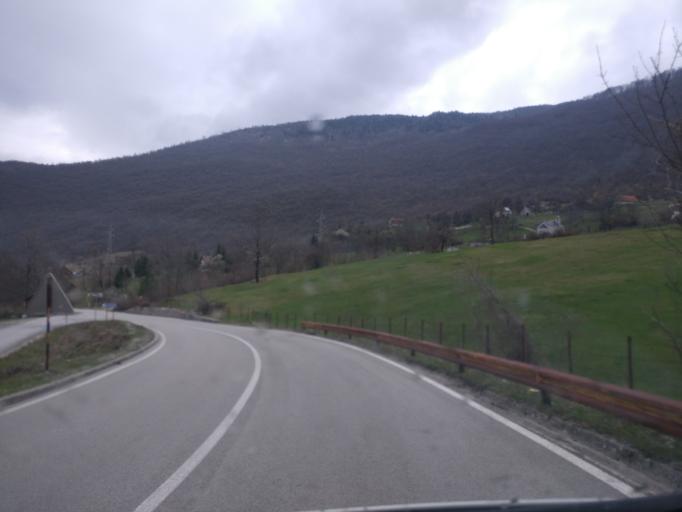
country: ME
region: Opstina Pluzine
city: Pluzine
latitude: 43.1127
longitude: 18.8152
